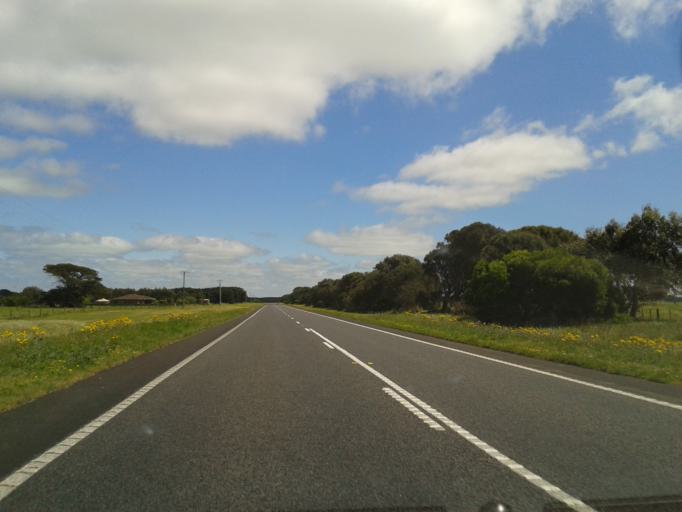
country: AU
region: Victoria
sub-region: Moyne
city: Port Fairy
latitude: -38.3067
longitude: 142.0407
